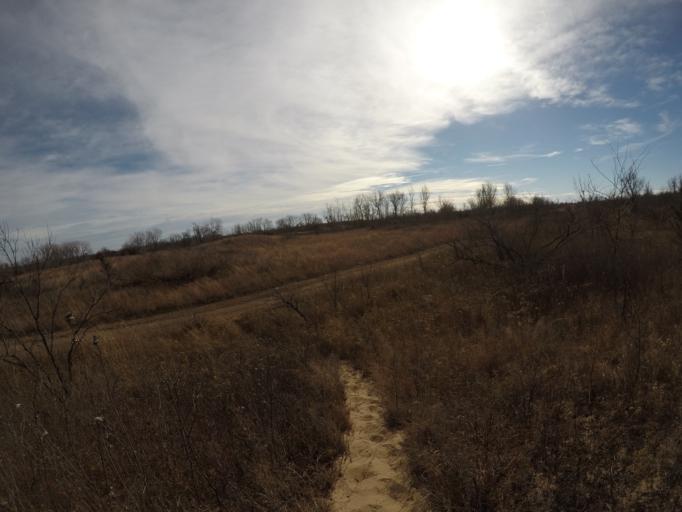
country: US
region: Kansas
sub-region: Reno County
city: Buhler
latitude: 38.1243
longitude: -97.8554
